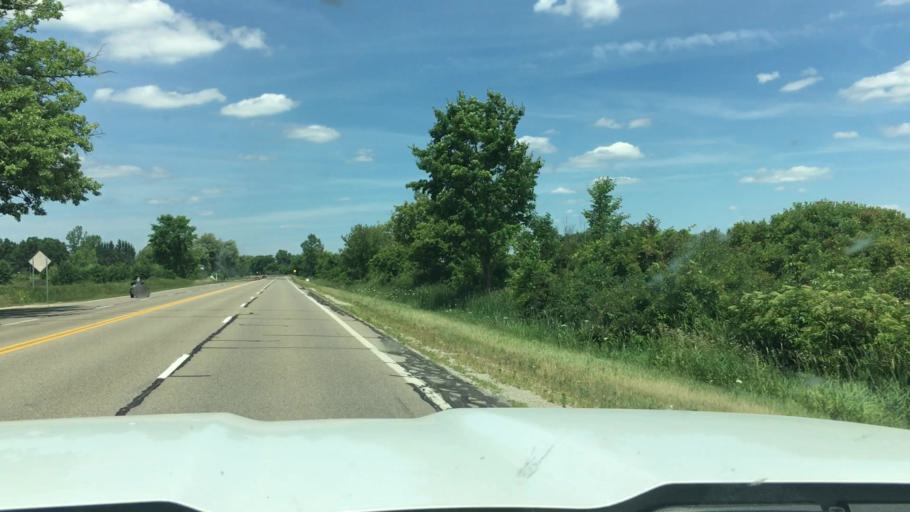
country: US
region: Michigan
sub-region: Lapeer County
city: Barnes Lake-Millers Lake
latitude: 43.2271
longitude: -83.3136
